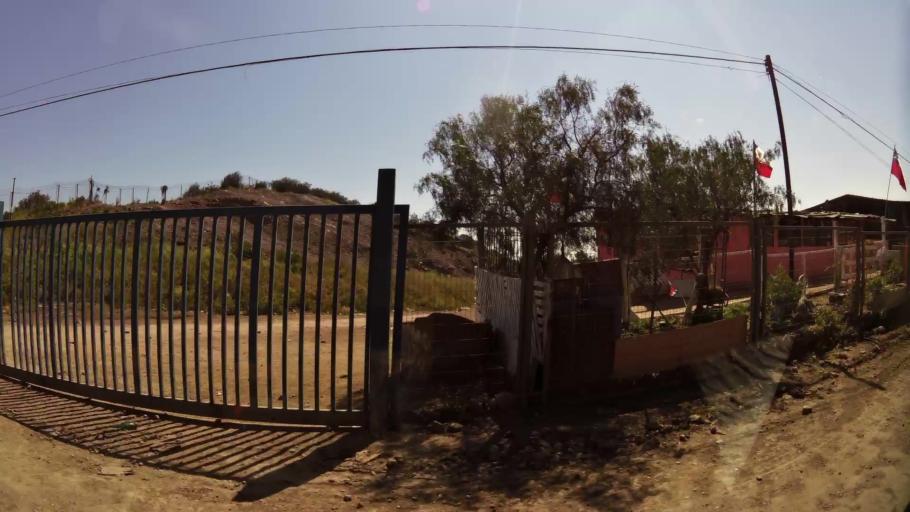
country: CL
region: Santiago Metropolitan
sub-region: Provincia de Santiago
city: Lo Prado
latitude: -33.3883
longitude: -70.7493
